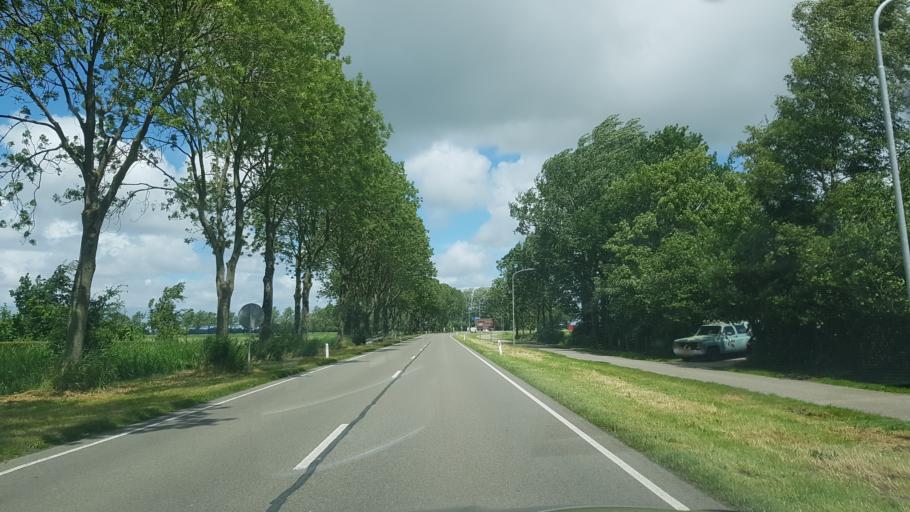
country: NL
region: Groningen
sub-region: Gemeente Winsum
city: Winsum
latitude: 53.3682
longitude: 6.5134
